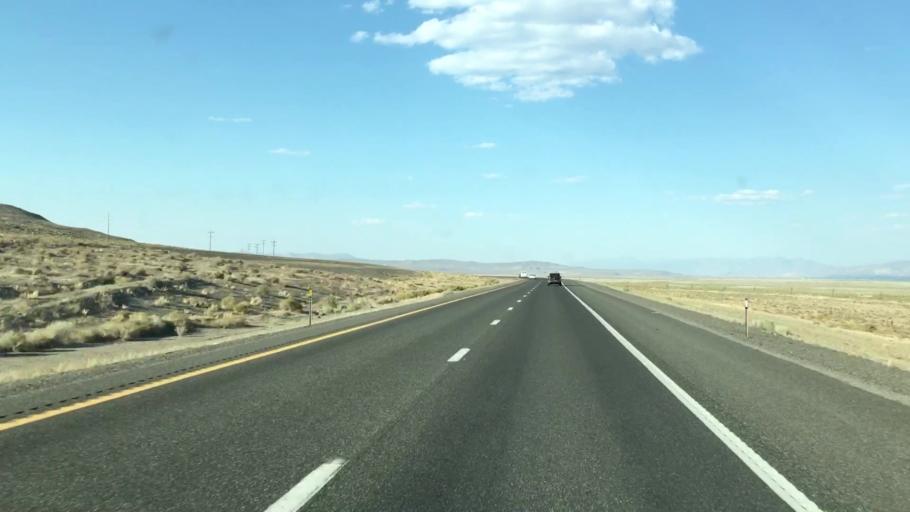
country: US
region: Nevada
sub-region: Pershing County
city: Lovelock
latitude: 39.9846
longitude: -118.6866
